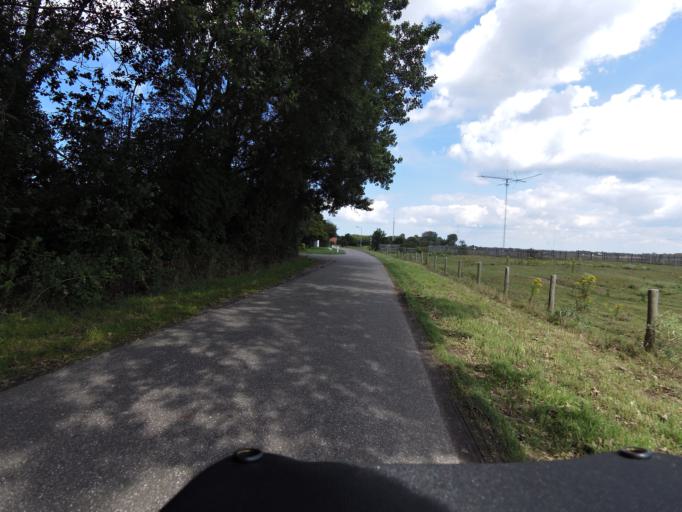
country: NL
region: South Holland
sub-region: Gemeente Goeree-Overflakkee
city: Ouddorp
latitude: 51.8078
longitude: 3.8876
